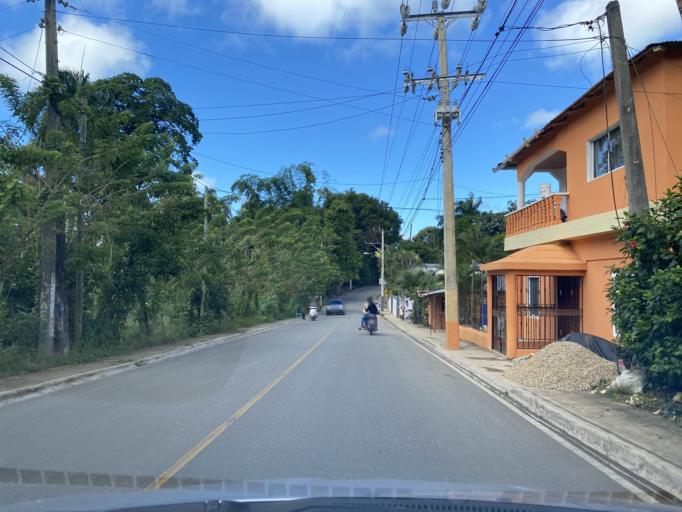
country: DO
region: Samana
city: Las Terrenas
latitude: 19.2901
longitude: -69.5480
